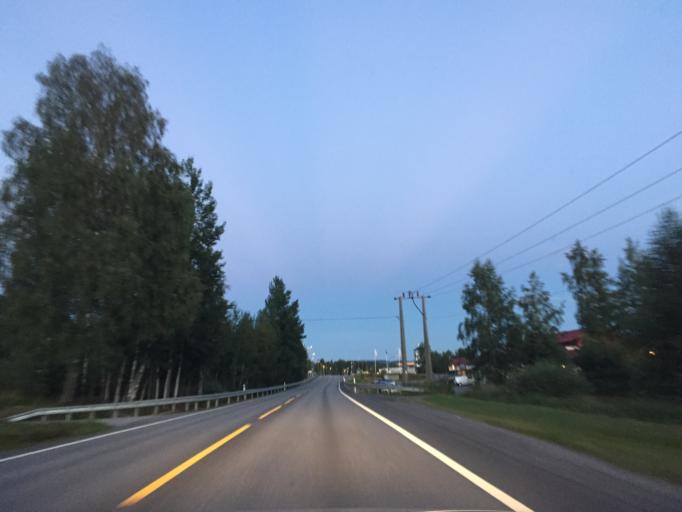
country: NO
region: Hedmark
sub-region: Kongsvinger
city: Kongsvinger
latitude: 60.2102
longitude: 11.9629
